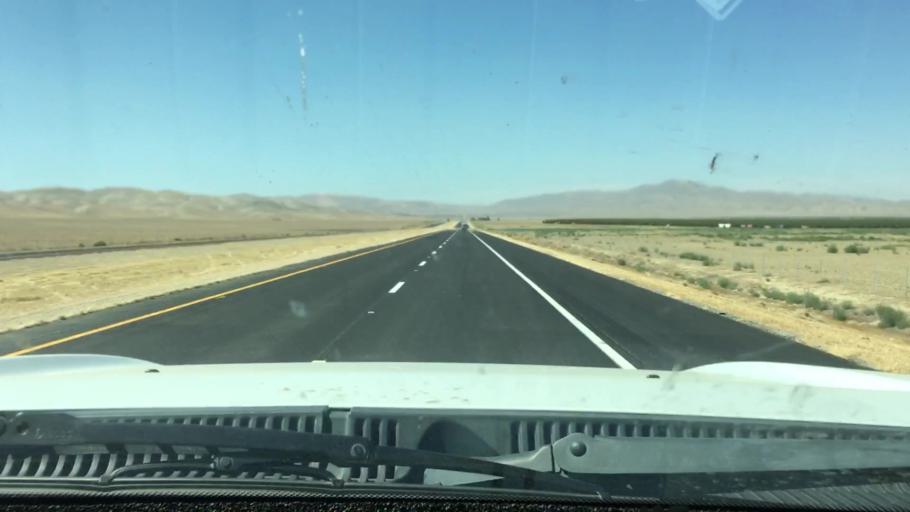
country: US
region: California
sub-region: Kern County
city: Lost Hills
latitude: 35.6221
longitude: -119.9797
